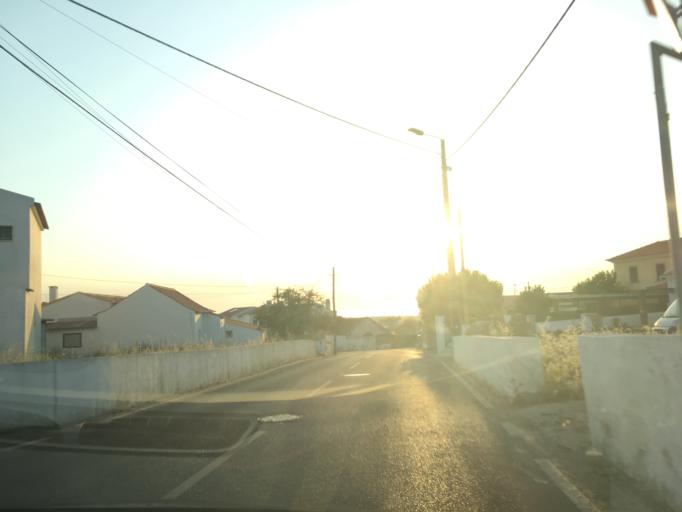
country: PT
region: Lisbon
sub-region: Sintra
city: Colares
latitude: 38.8263
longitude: -9.4357
